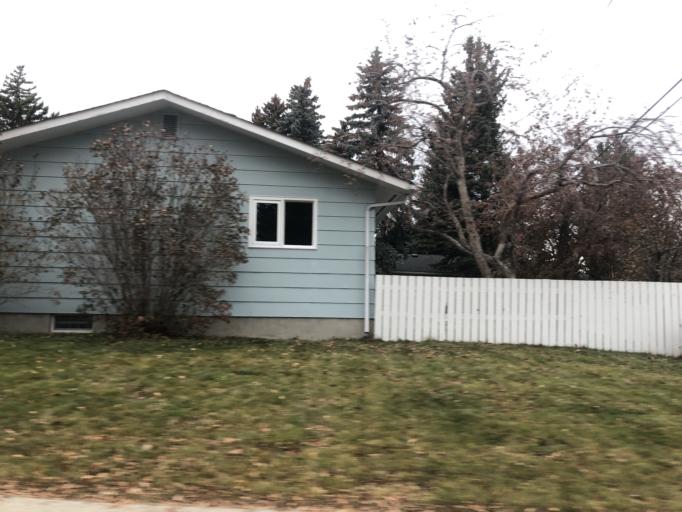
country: CA
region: Alberta
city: Calgary
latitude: 50.9465
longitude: -114.0499
